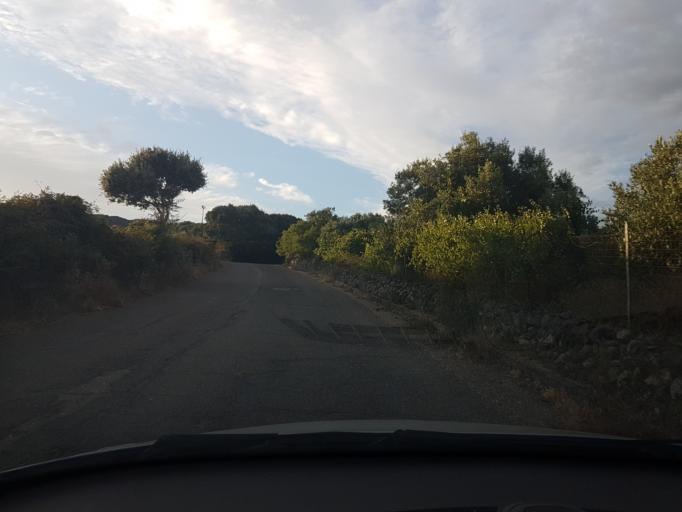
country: IT
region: Sardinia
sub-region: Provincia di Oristano
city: Seneghe
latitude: 40.1043
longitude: 8.6222
